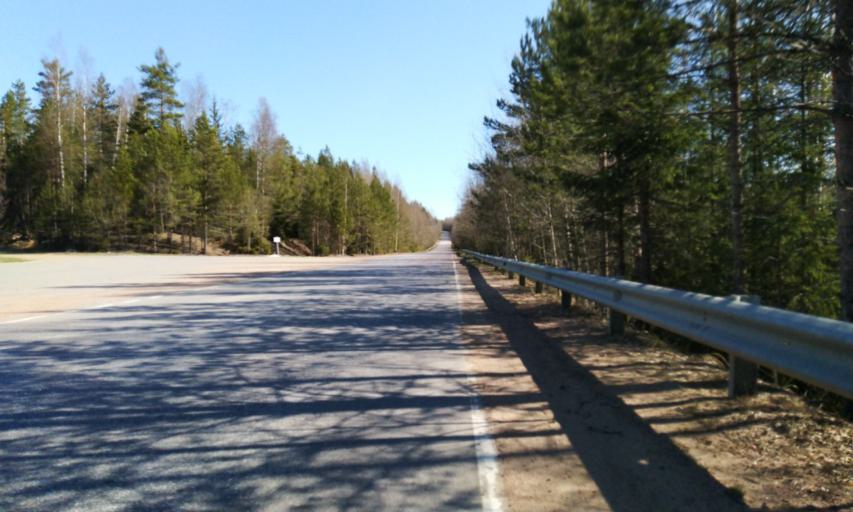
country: RU
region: Leningrad
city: Garbolovo
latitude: 60.3804
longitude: 30.4643
